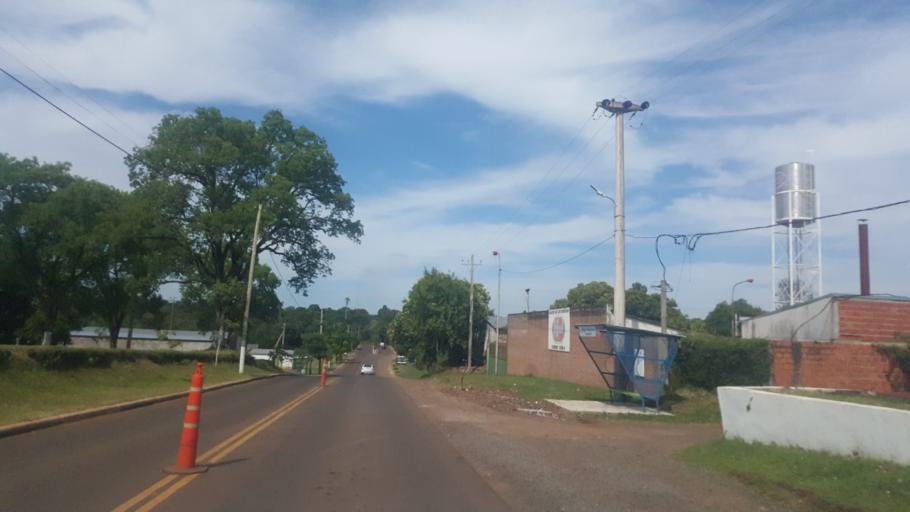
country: AR
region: Misiones
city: Cerro Cora
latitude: -27.5119
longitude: -55.6084
